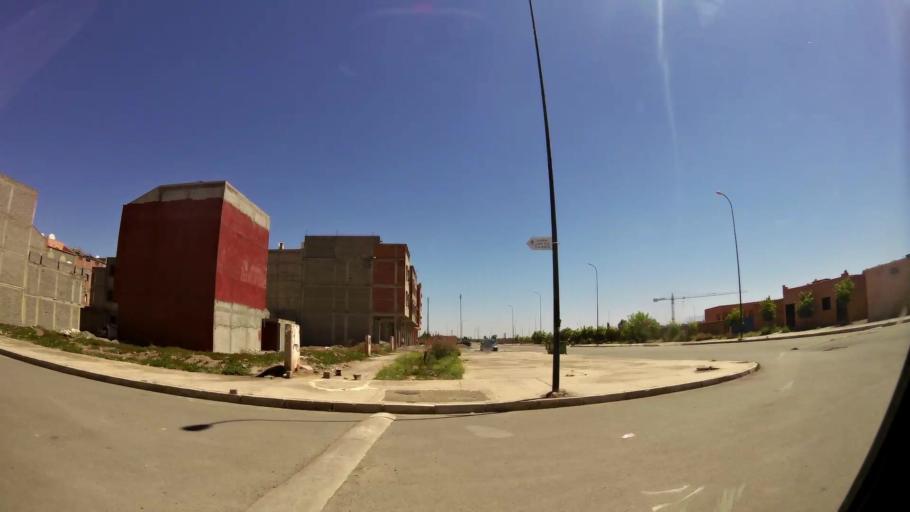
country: MA
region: Marrakech-Tensift-Al Haouz
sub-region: Marrakech
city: Marrakesh
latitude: 31.5526
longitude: -7.9786
